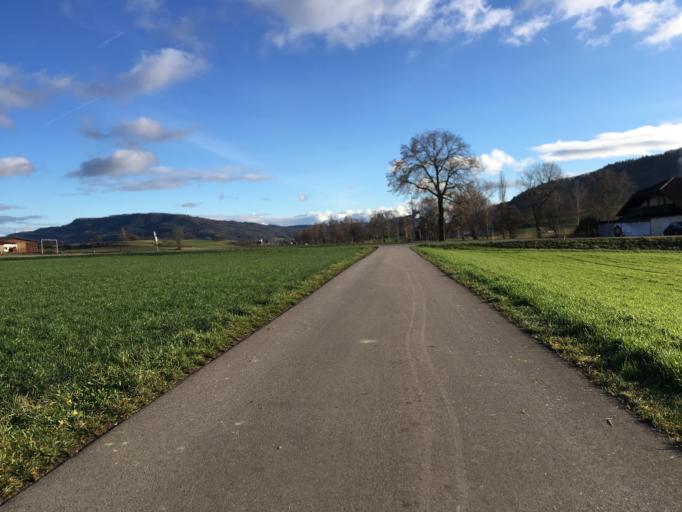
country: DE
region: Baden-Wuerttemberg
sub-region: Freiburg Region
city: Gottmadingen
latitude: 47.7190
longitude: 8.7853
